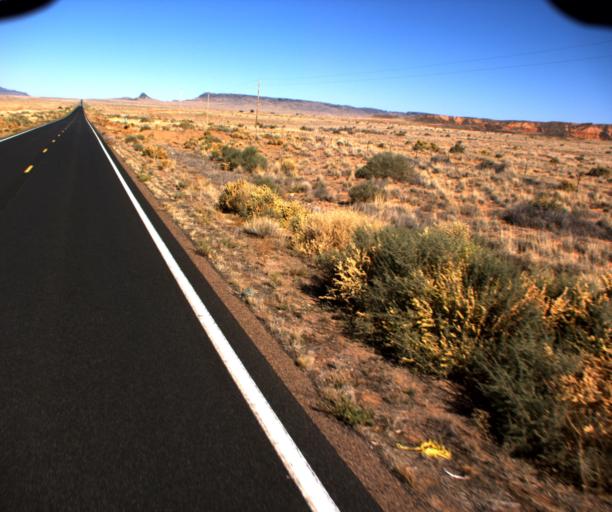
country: US
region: Arizona
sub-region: Navajo County
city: Dilkon
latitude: 35.3299
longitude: -110.4234
